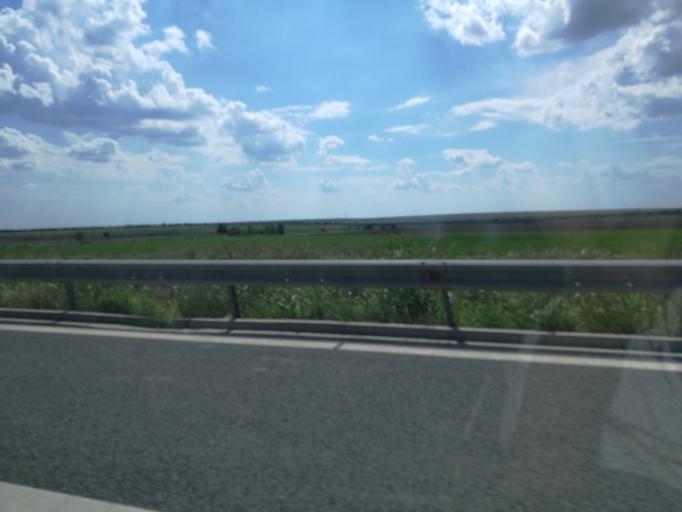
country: RO
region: Constanta
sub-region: Municipiul Constanta
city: Palazu Mare
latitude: 44.2105
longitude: 28.5528
